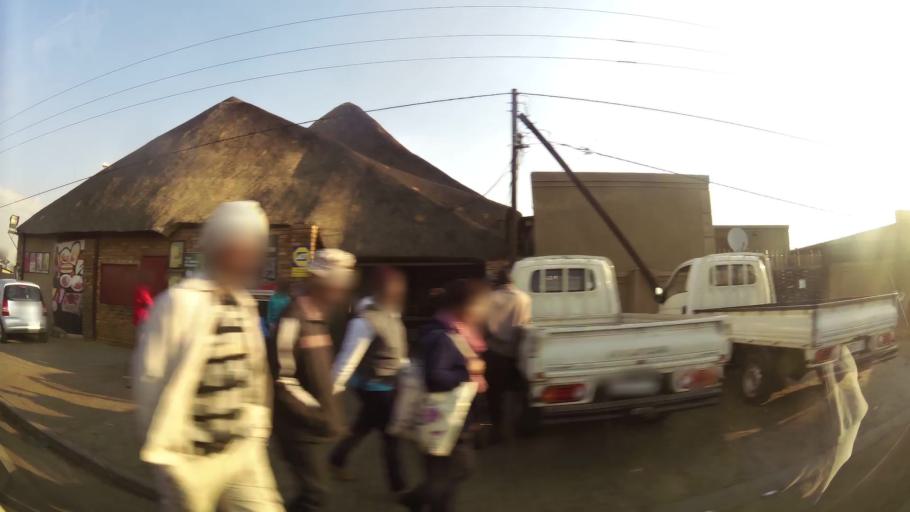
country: ZA
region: Gauteng
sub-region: Ekurhuleni Metropolitan Municipality
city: Boksburg
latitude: -26.2930
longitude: 28.2735
